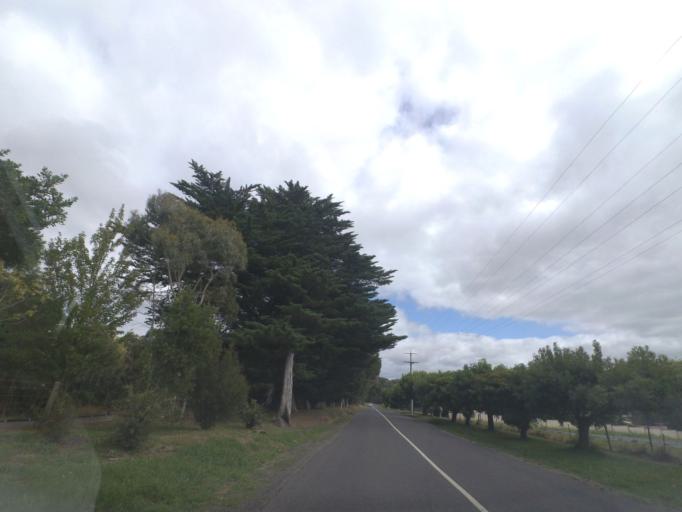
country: AU
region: Victoria
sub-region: Yarra Ranges
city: Woori Yallock
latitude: -37.8064
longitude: 145.4857
